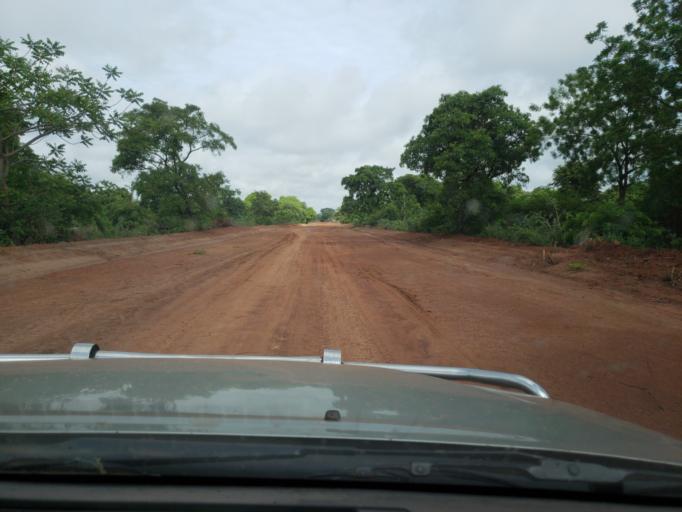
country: ML
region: Sikasso
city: Koutiala
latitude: 12.3925
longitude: -6.0191
